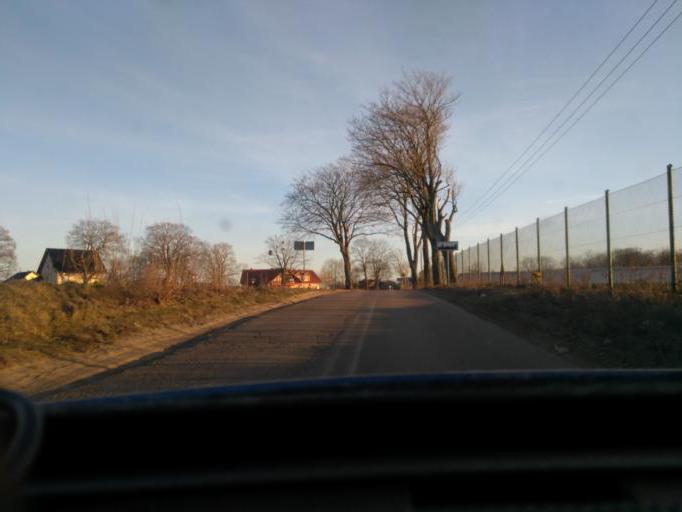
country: PL
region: Pomeranian Voivodeship
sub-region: Powiat kartuski
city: Przodkowo
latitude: 54.4034
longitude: 18.3306
